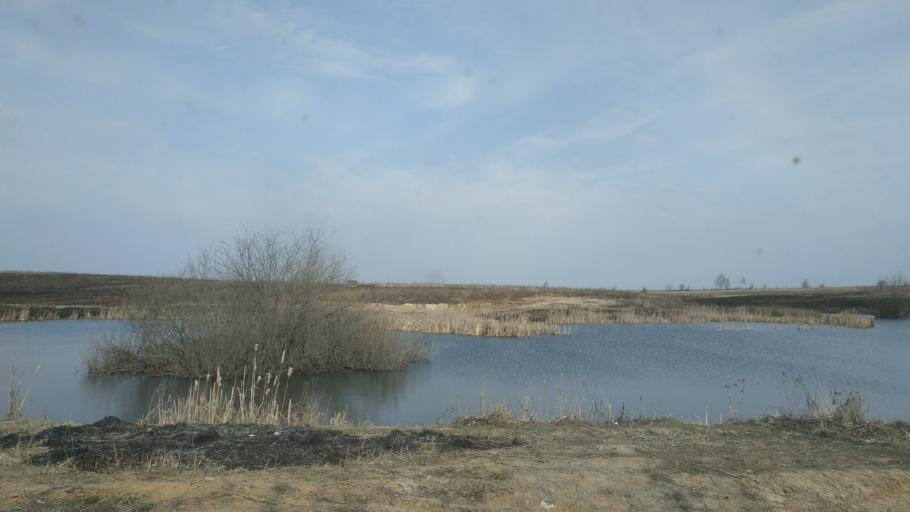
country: RU
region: Moskovskaya
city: Troitskoye
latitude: 55.3591
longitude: 38.4601
